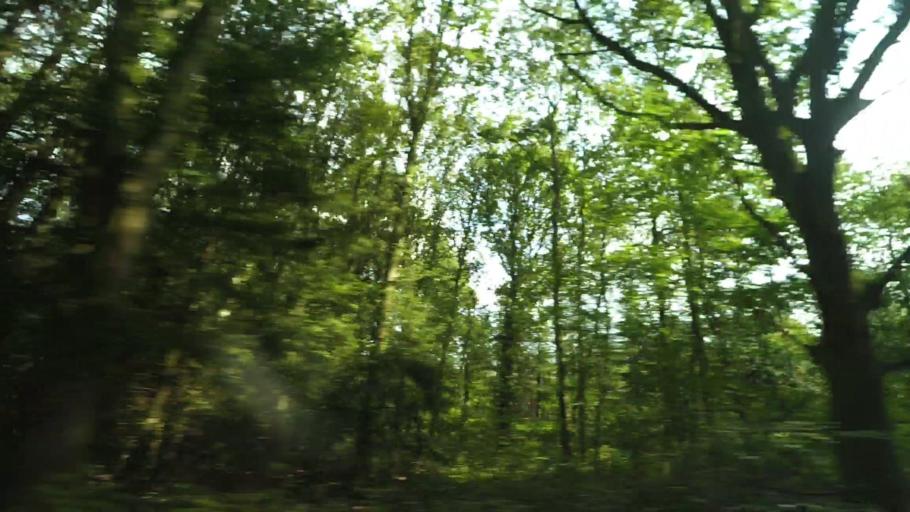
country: DK
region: Central Jutland
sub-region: Syddjurs Kommune
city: Ryomgard
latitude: 56.4599
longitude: 10.5361
